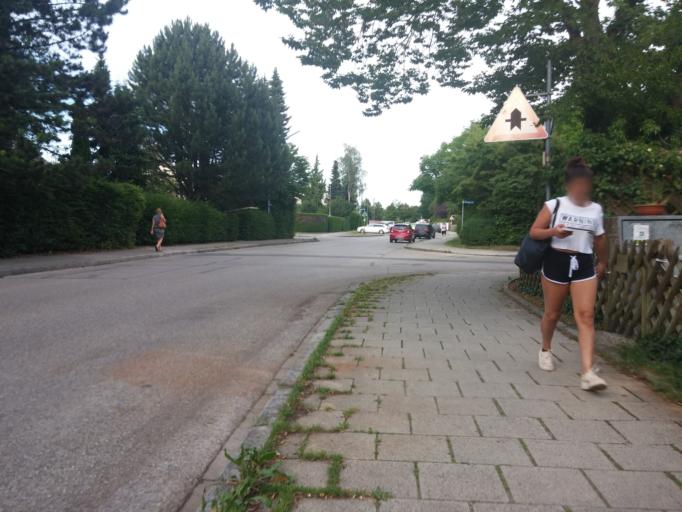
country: DE
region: Bavaria
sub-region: Upper Bavaria
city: Haar
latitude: 48.1039
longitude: 11.7264
